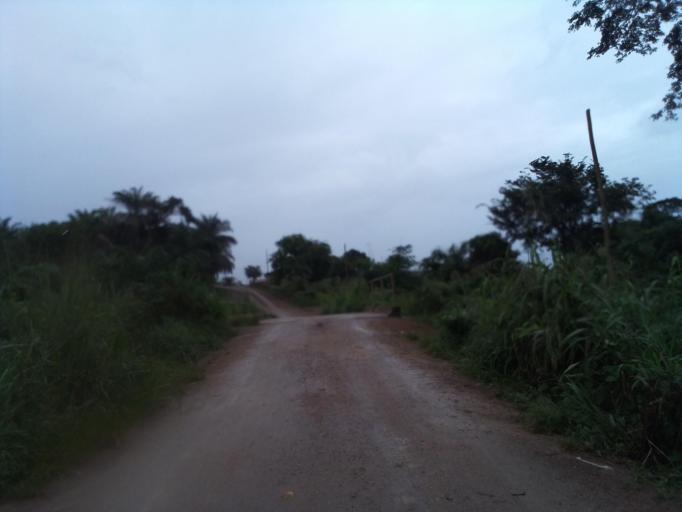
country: SL
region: Eastern Province
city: Kenema
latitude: 7.8771
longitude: -11.1579
